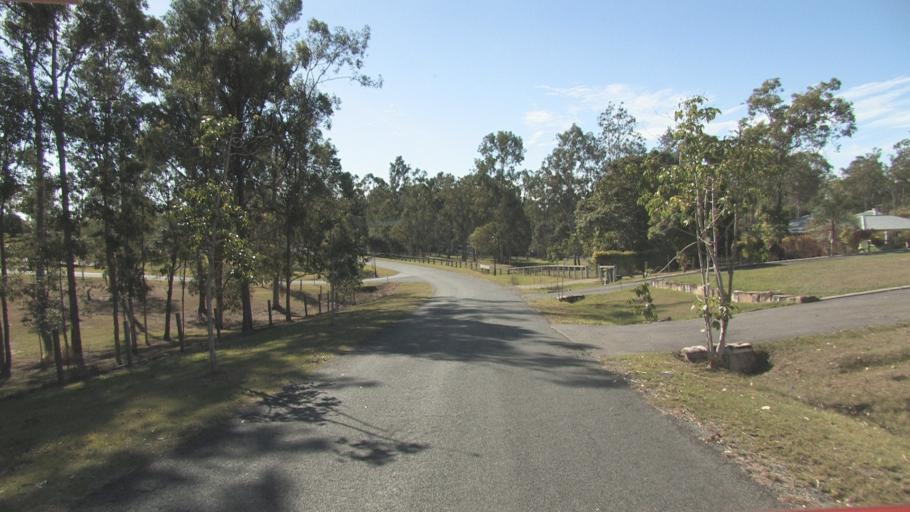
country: AU
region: Queensland
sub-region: Ipswich
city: Springfield Lakes
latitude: -27.7326
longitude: 152.9288
